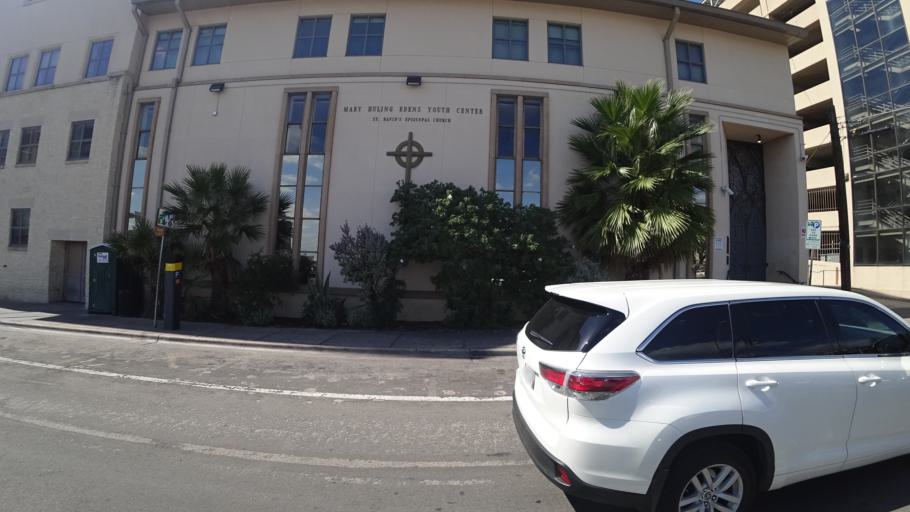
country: US
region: Texas
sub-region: Travis County
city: Austin
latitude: 30.2684
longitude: -97.7389
